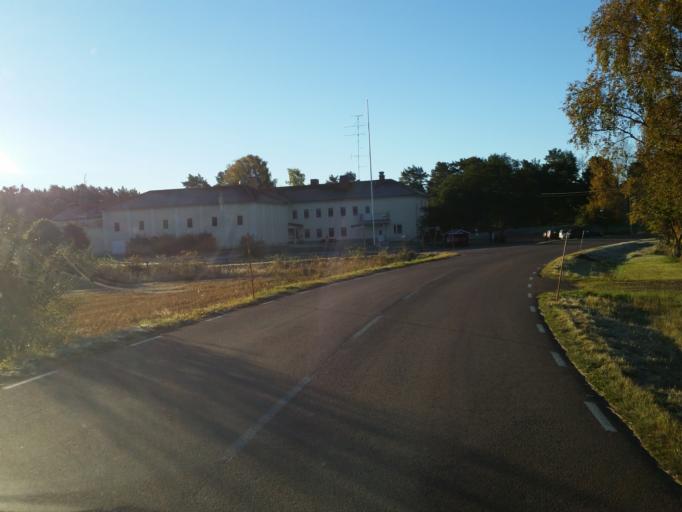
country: AX
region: Alands skaergard
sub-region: Vardoe
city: Vardoe
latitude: 60.2453
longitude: 20.3754
